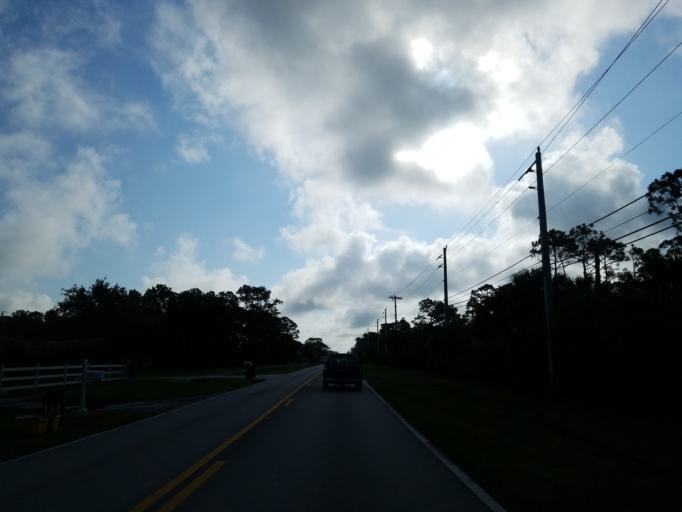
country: US
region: Florida
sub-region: Martin County
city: Palm City
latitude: 27.1253
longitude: -80.2493
